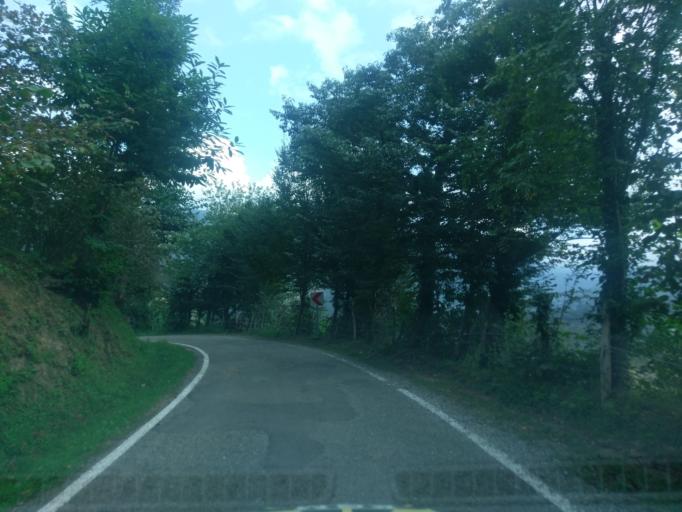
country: TR
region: Ordu
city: Camas
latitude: 40.9258
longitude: 37.6089
